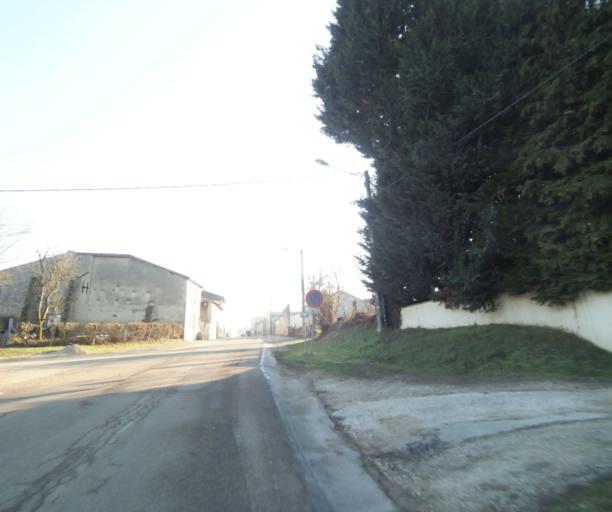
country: FR
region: Champagne-Ardenne
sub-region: Departement de la Haute-Marne
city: Bienville
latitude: 48.5864
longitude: 5.0859
